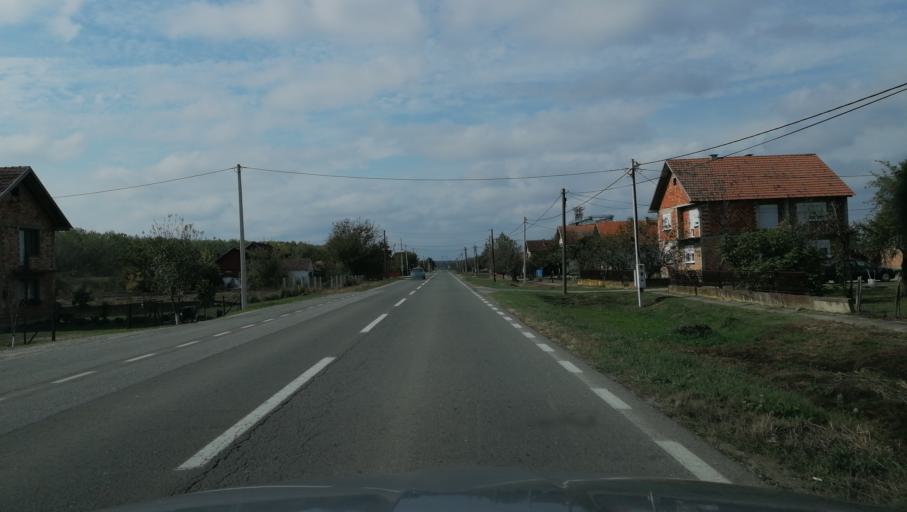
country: RS
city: Bosut
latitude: 44.9243
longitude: 19.3416
